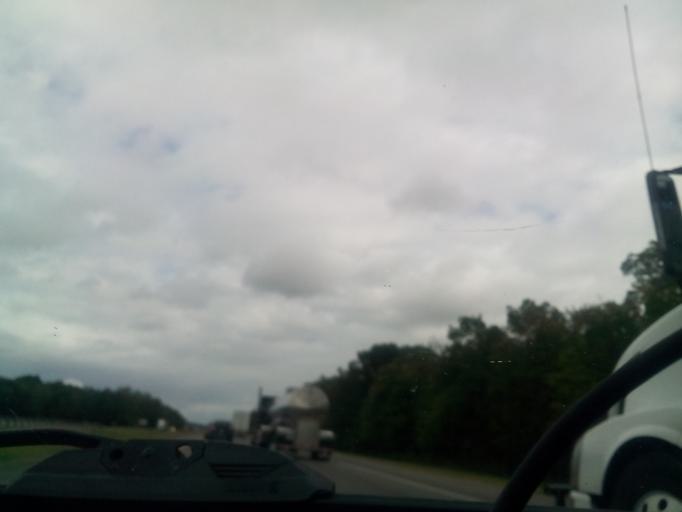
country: US
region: Ohio
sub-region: Williams County
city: Montpelier
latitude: 41.6286
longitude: -84.7428
